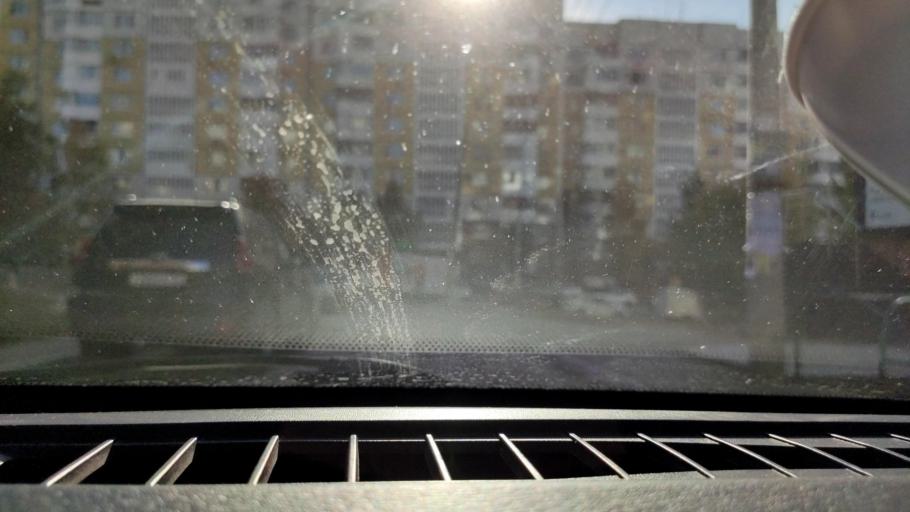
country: RU
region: Samara
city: Samara
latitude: 53.2654
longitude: 50.2166
